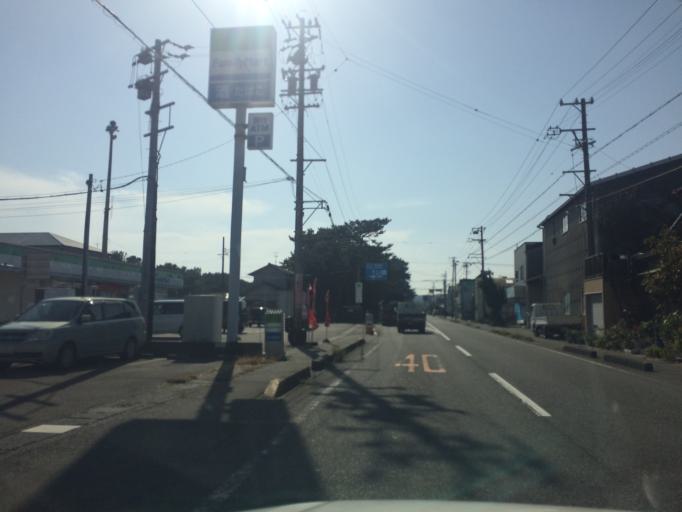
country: JP
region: Shizuoka
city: Sagara
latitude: 34.6803
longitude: 138.2010
